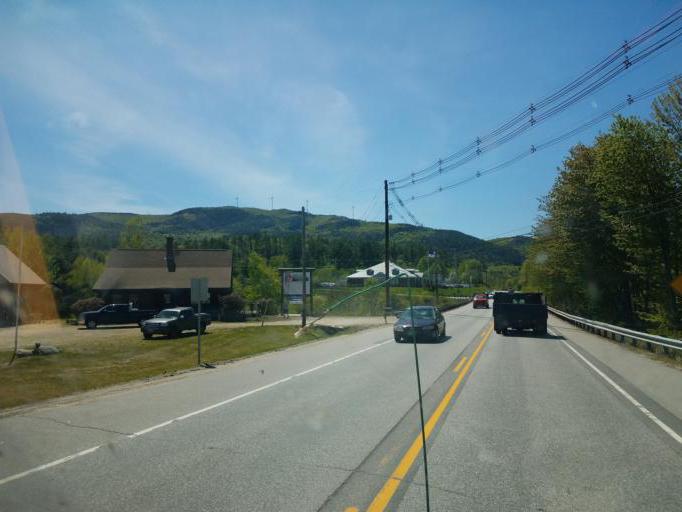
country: US
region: New Hampshire
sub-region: Grafton County
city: Plymouth
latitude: 43.7709
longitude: -71.7513
